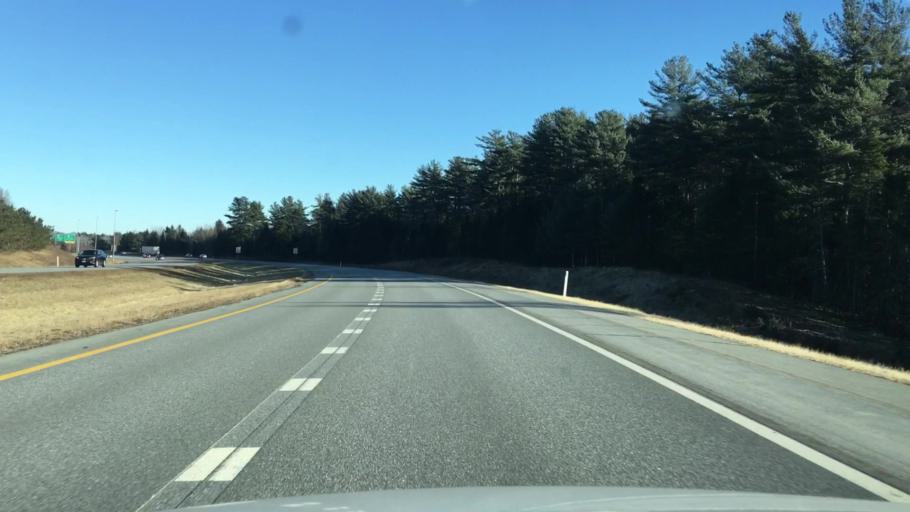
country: US
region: Maine
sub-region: Penobscot County
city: Brewer
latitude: 44.7676
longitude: -68.7319
